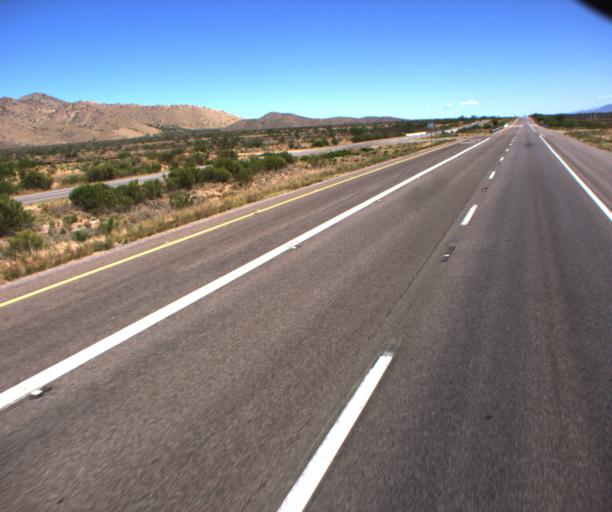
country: US
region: Arizona
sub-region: Cochise County
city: Whetstone
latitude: 31.8144
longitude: -110.3477
